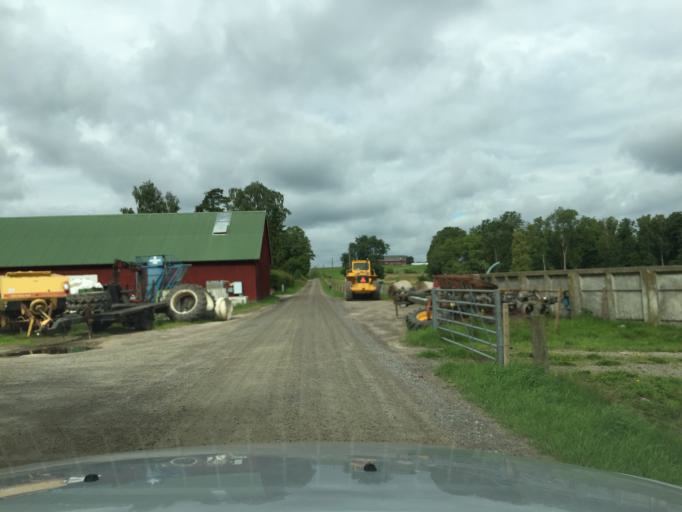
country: SE
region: Skane
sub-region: Hassleholms Kommun
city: Sosdala
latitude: 56.0302
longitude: 13.6646
